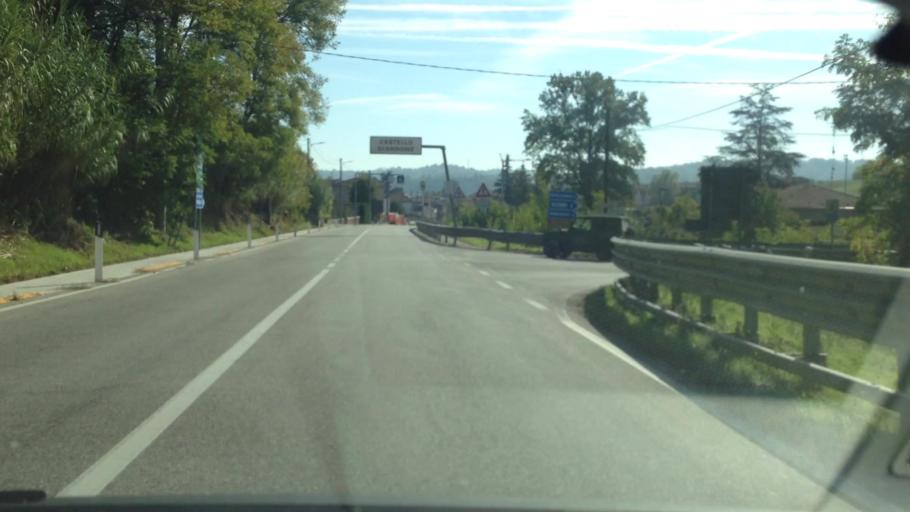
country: IT
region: Piedmont
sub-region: Provincia di Asti
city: Castello di Annone
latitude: 44.8838
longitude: 8.3113
